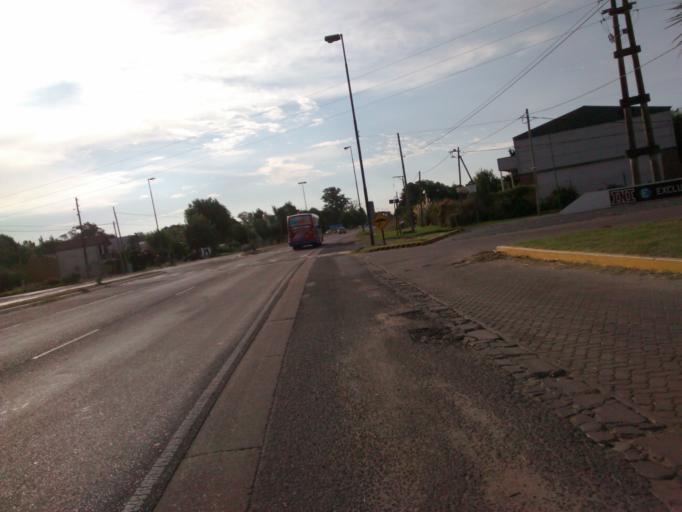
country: AR
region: Buenos Aires
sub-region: Partido de La Plata
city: La Plata
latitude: -34.8497
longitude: -58.0939
